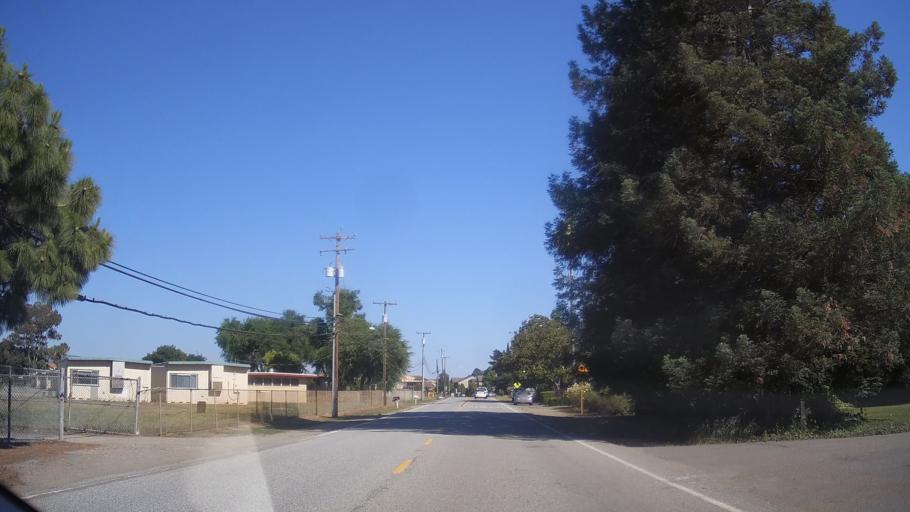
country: US
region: California
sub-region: Santa Clara County
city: Morgan Hill
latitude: 37.1548
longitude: -121.6808
